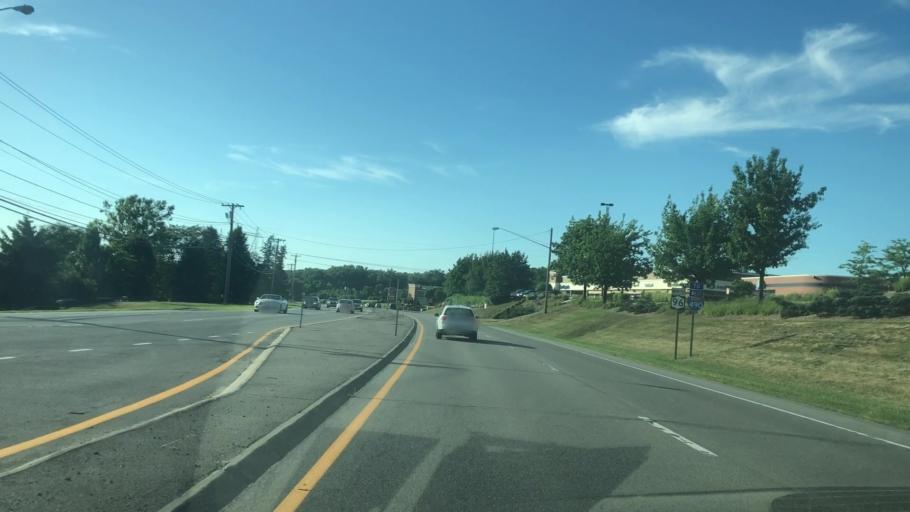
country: US
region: New York
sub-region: Ontario County
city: Victor
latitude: 43.0298
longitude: -77.4397
